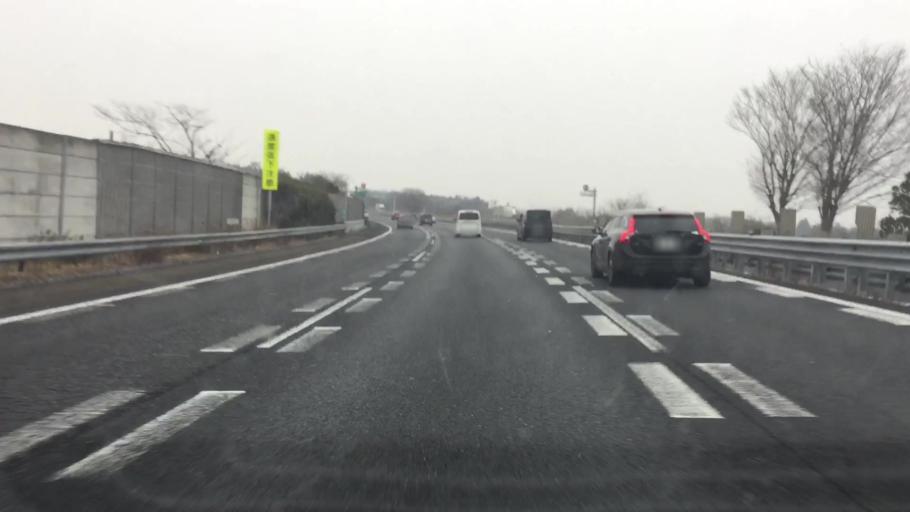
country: JP
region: Tochigi
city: Tochigi
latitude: 36.3912
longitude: 139.6850
